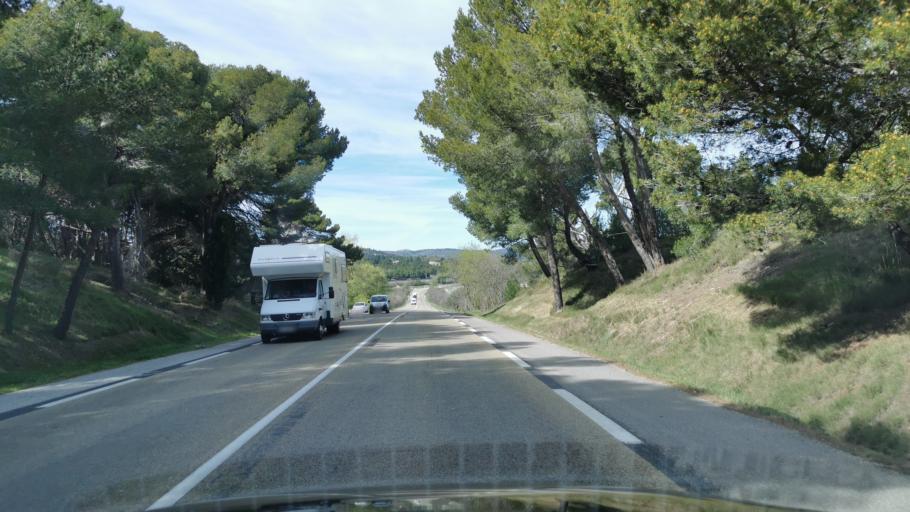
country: FR
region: Languedoc-Roussillon
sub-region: Departement de l'Aude
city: Portel-des-Corbieres
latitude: 43.0578
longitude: 2.9419
